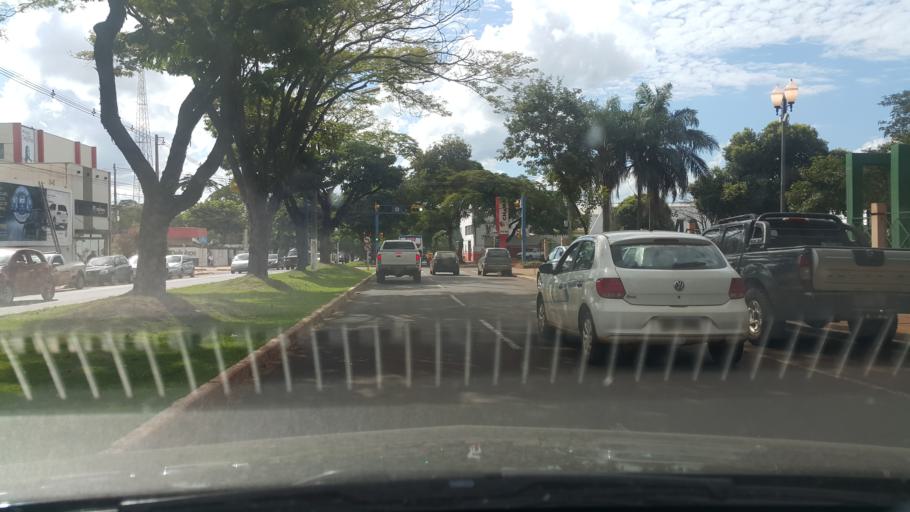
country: BR
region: Mato Grosso do Sul
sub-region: Dourados
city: Dourados
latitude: -22.2176
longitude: -54.8130
